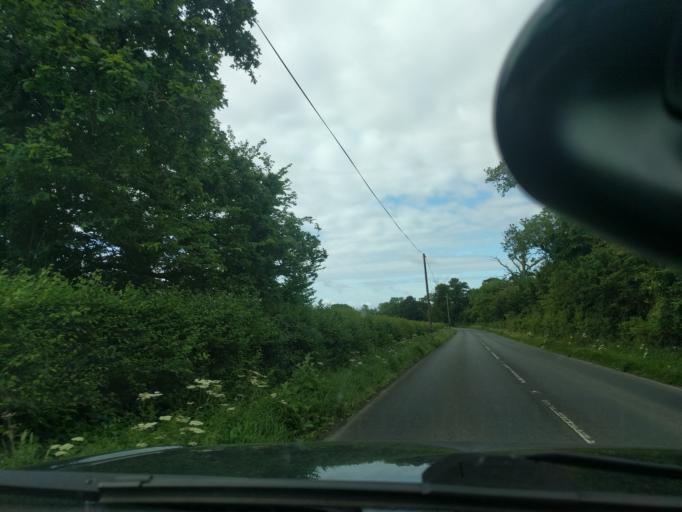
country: GB
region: England
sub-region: Wiltshire
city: Calne
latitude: 51.4660
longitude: -1.9842
